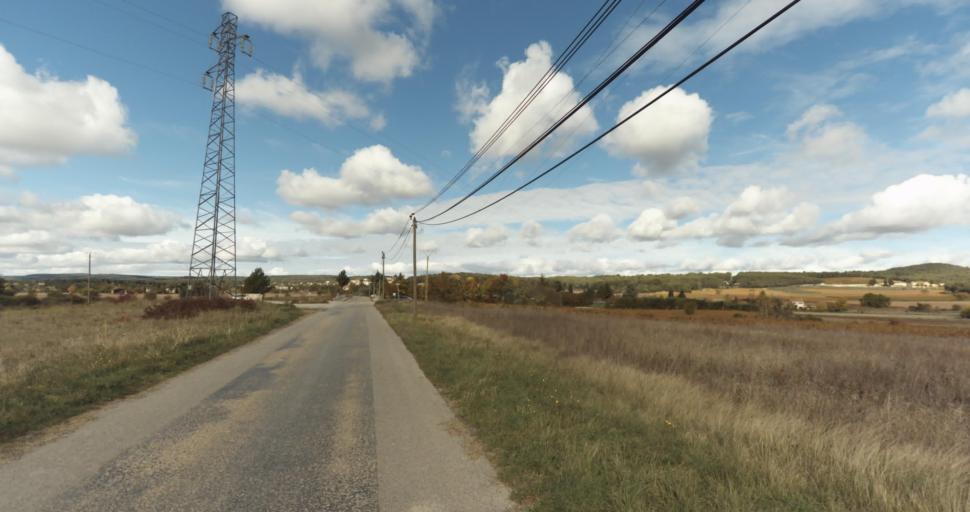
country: FR
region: Provence-Alpes-Cote d'Azur
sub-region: Departement des Bouches-du-Rhone
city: Venelles
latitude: 43.5824
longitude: 5.4938
